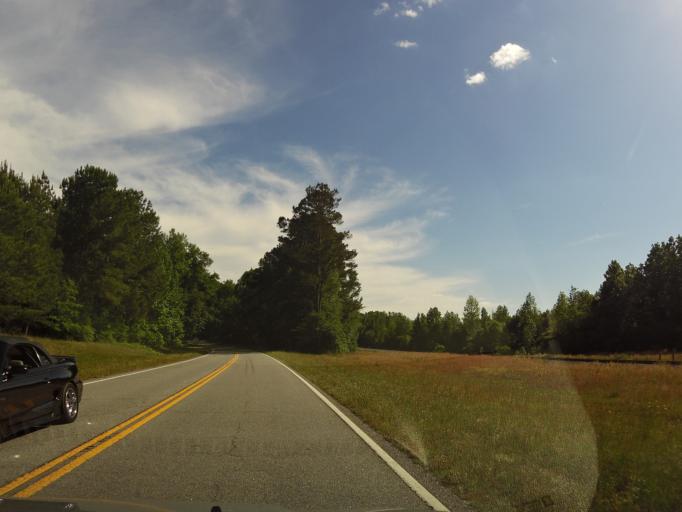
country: US
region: South Carolina
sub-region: Bamberg County
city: Denmark
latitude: 33.1563
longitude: -81.1932
